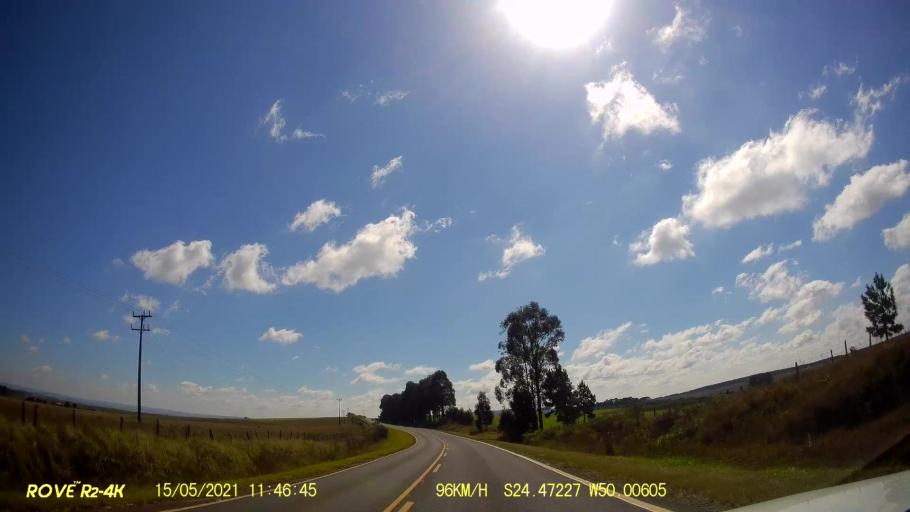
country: BR
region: Parana
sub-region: Pirai Do Sul
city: Pirai do Sul
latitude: -24.4723
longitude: -50.0061
